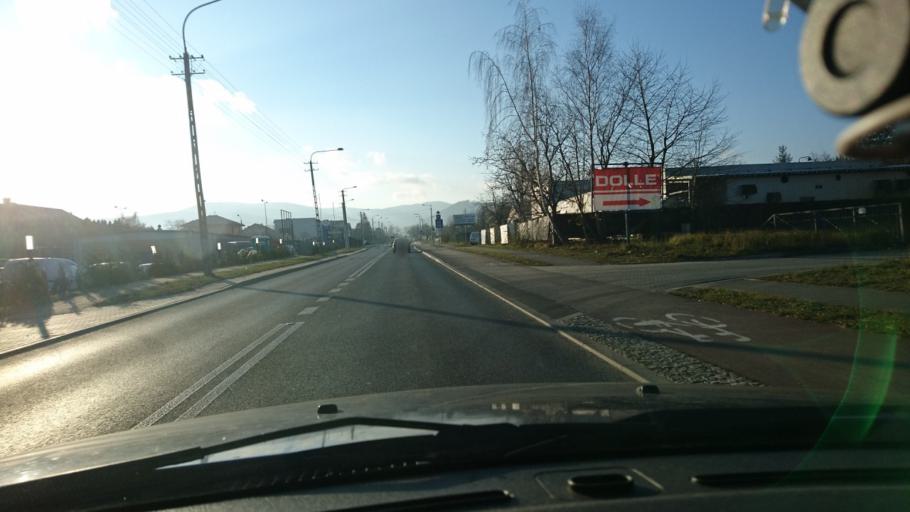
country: PL
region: Silesian Voivodeship
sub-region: Powiat bielski
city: Jaworze
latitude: 49.8192
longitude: 18.9753
